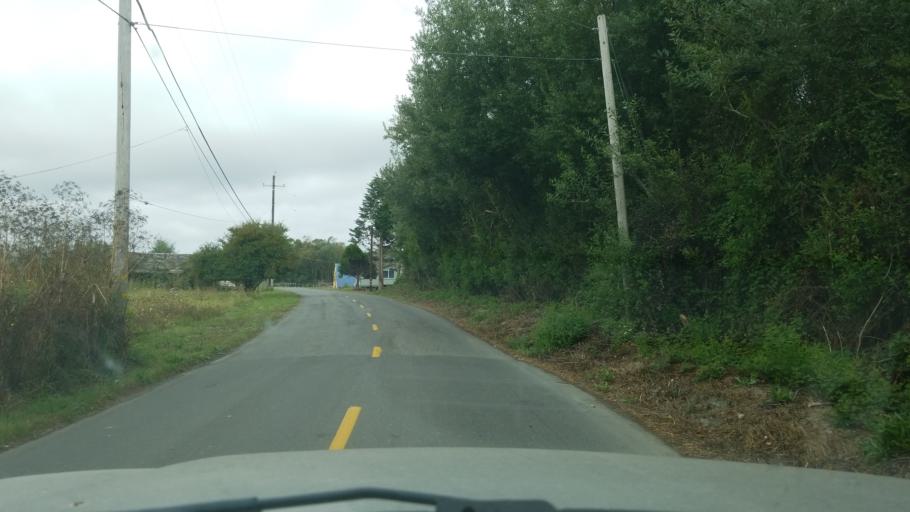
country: US
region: California
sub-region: Humboldt County
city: Ferndale
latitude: 40.5941
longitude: -124.2647
